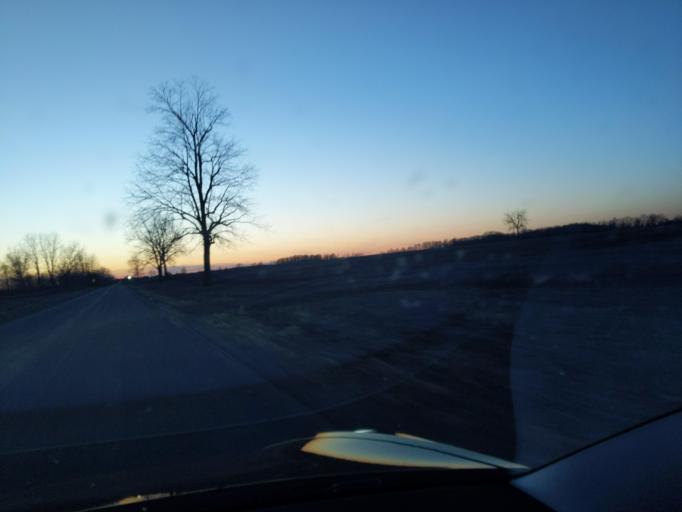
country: US
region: Michigan
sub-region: Ingham County
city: Stockbridge
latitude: 42.5188
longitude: -84.1982
